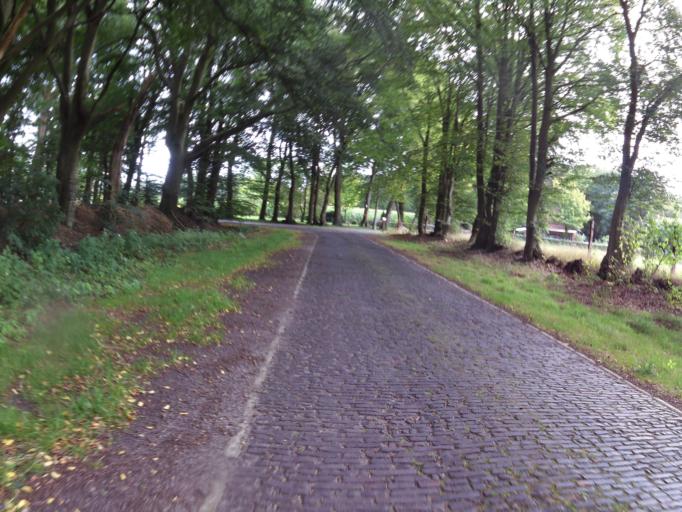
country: DE
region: Lower Saxony
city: Kohlen
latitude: 53.5037
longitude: 8.9135
